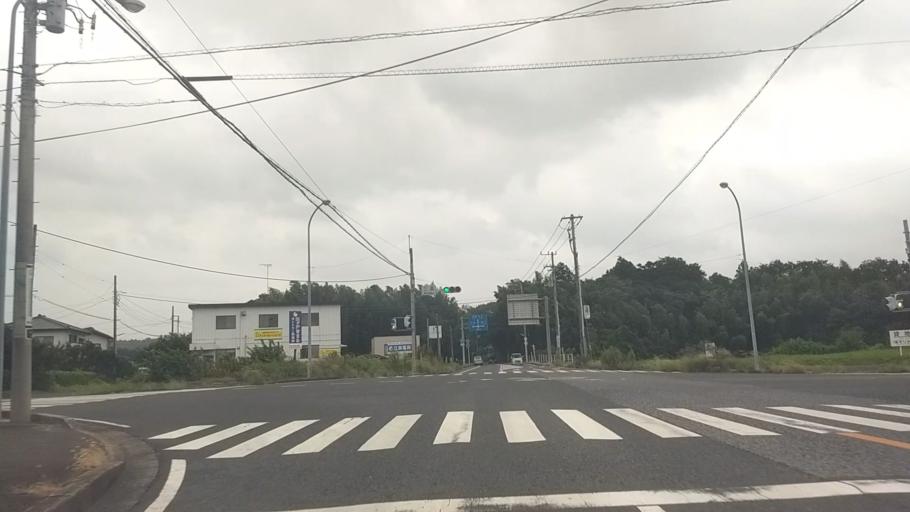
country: JP
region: Chiba
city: Ichihara
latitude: 35.3880
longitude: 140.0572
